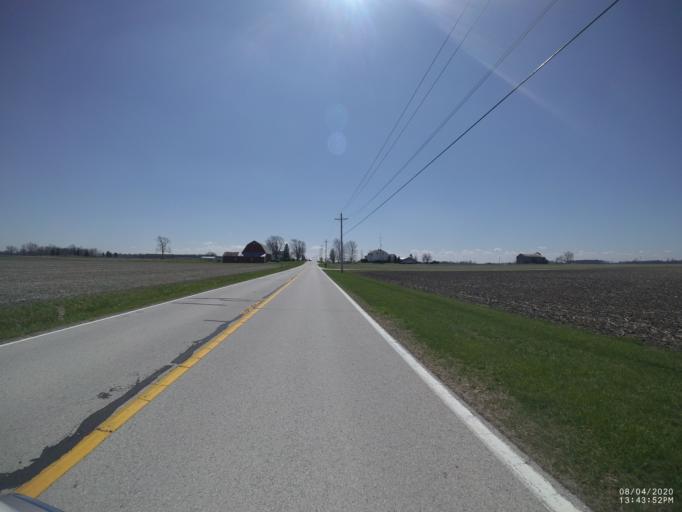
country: US
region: Ohio
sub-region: Sandusky County
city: Gibsonburg
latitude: 41.3301
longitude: -83.3059
